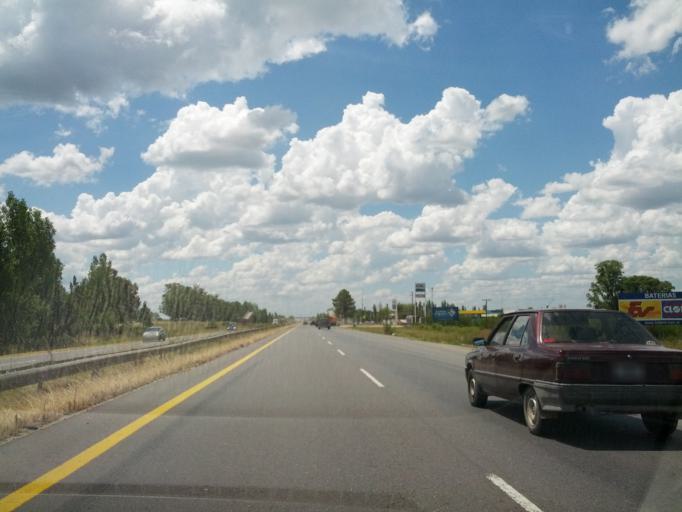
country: AR
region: Entre Rios
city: Gualeguaychu
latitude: -33.0531
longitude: -58.6239
